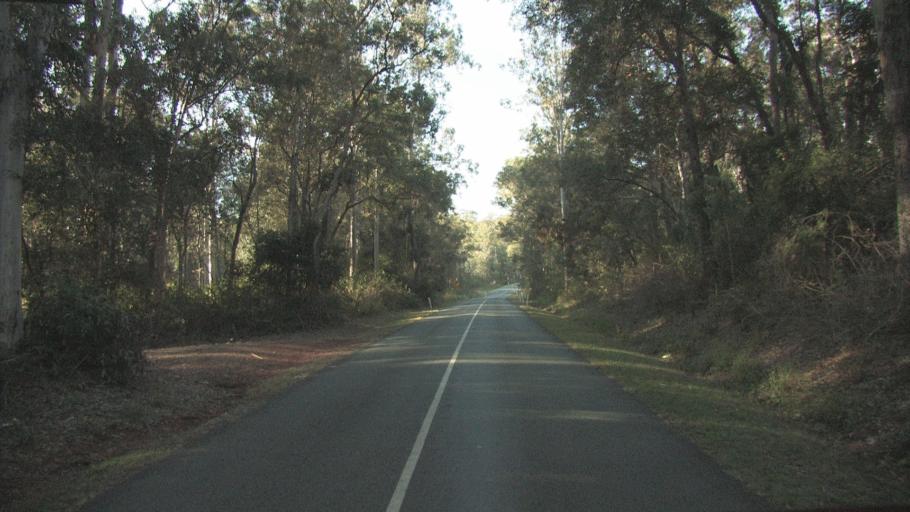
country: AU
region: Queensland
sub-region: Gold Coast
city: Ormeau Hills
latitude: -27.8427
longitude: 153.1567
